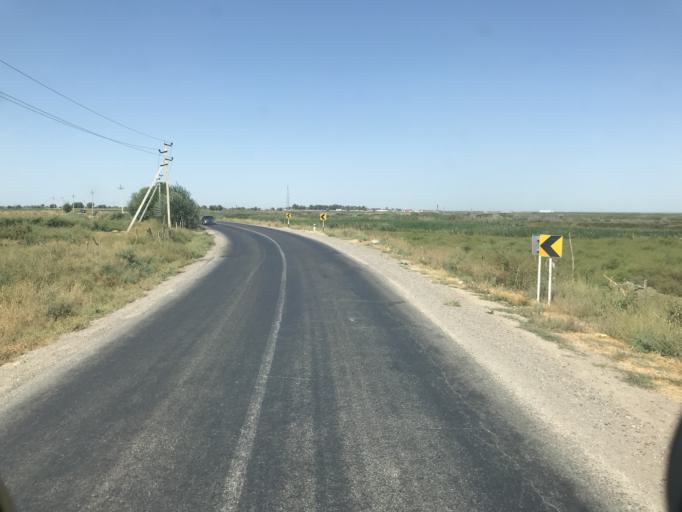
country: KZ
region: Ongtustik Qazaqstan
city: Ilyich
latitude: 40.9508
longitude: 68.4816
